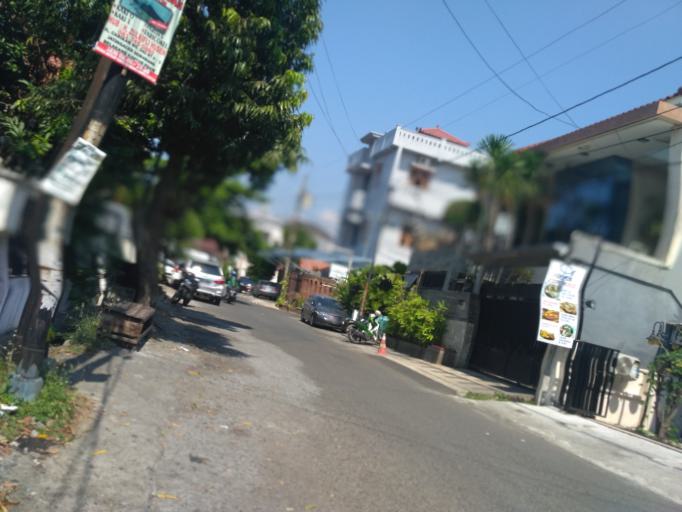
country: ID
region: Central Java
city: Semarang
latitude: -6.9988
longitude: 110.4260
